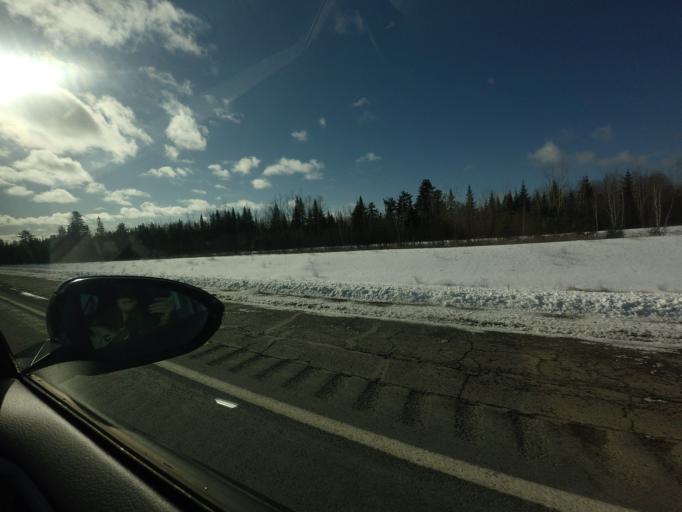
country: CA
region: New Brunswick
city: Fredericton
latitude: 45.8918
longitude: -66.6457
